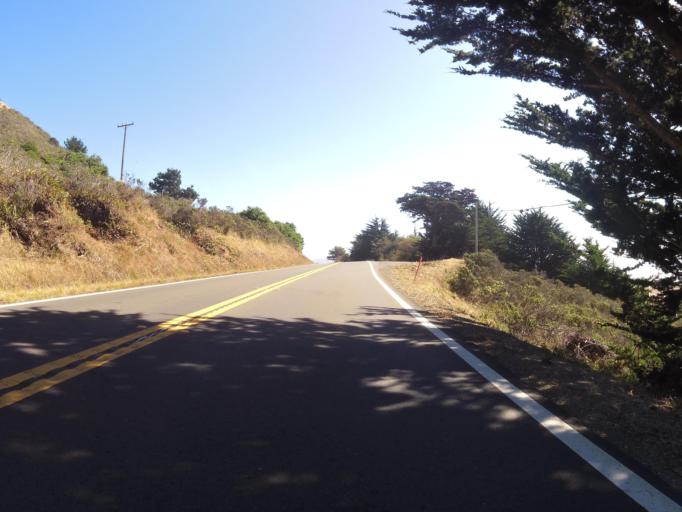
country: US
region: California
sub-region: Mendocino County
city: Fort Bragg
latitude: 39.5955
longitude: -123.7822
